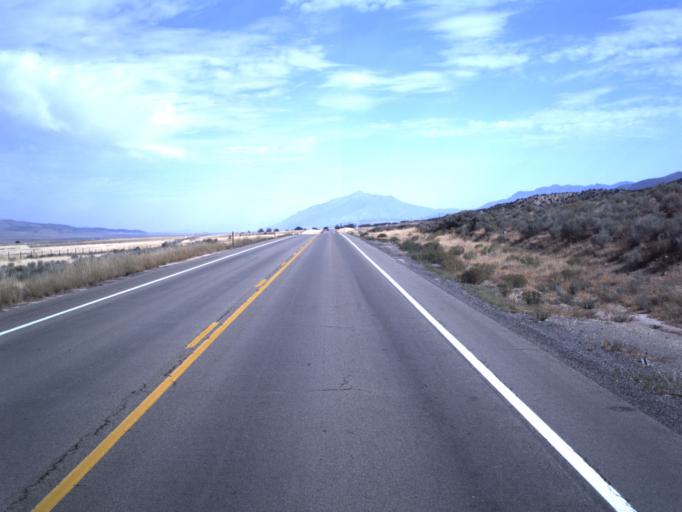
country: US
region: Utah
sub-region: Sanpete County
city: Gunnison
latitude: 39.4154
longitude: -111.9238
